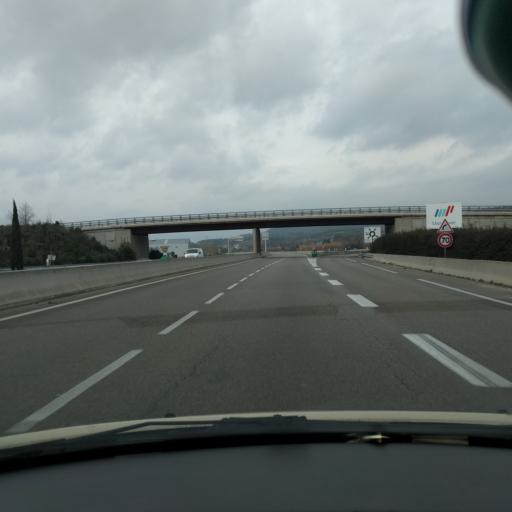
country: FR
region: Provence-Alpes-Cote d'Azur
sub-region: Departement des Bouches-du-Rhone
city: Meyreuil
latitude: 43.4733
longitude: 5.4829
